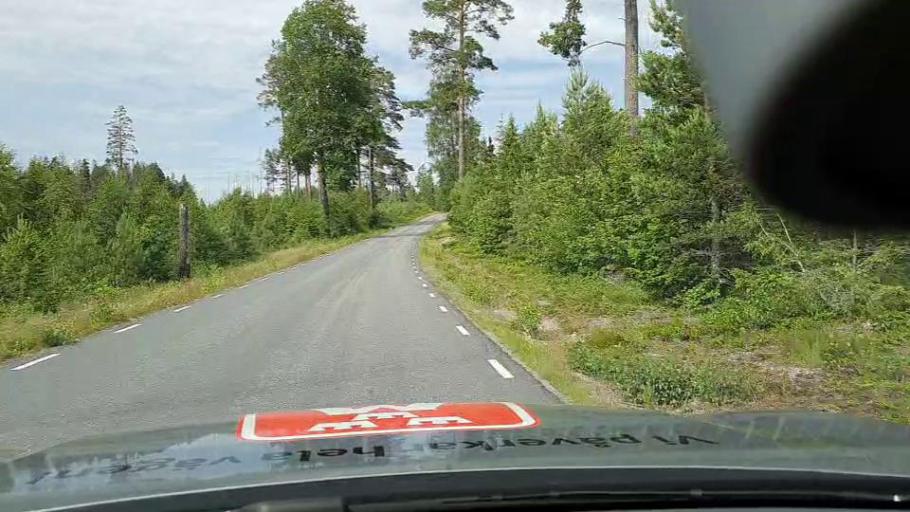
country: SE
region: Soedermanland
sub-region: Eskilstuna Kommun
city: Arla
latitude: 59.2375
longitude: 16.7224
